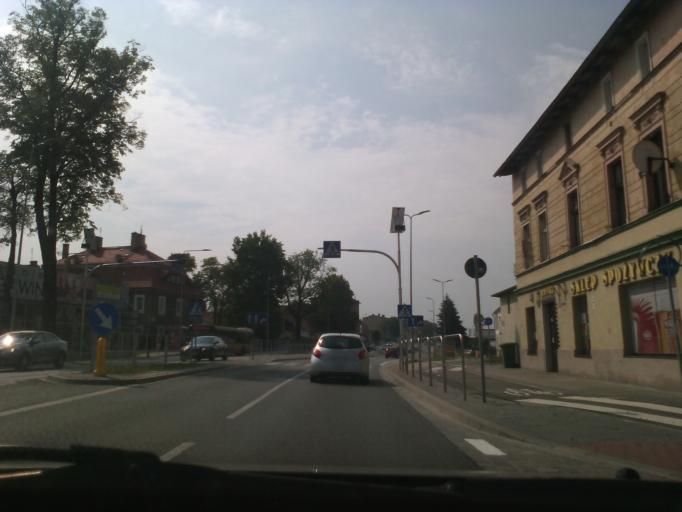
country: PL
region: Lower Silesian Voivodeship
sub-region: Powiat swidnicki
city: Swiebodzice
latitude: 50.8270
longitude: 16.3047
